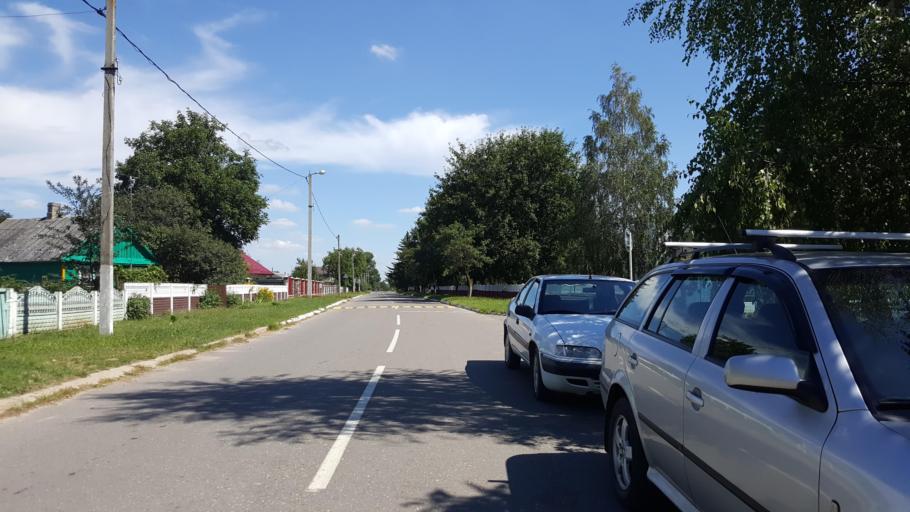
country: BY
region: Brest
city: Charnawchytsy
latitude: 52.2683
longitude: 23.5870
